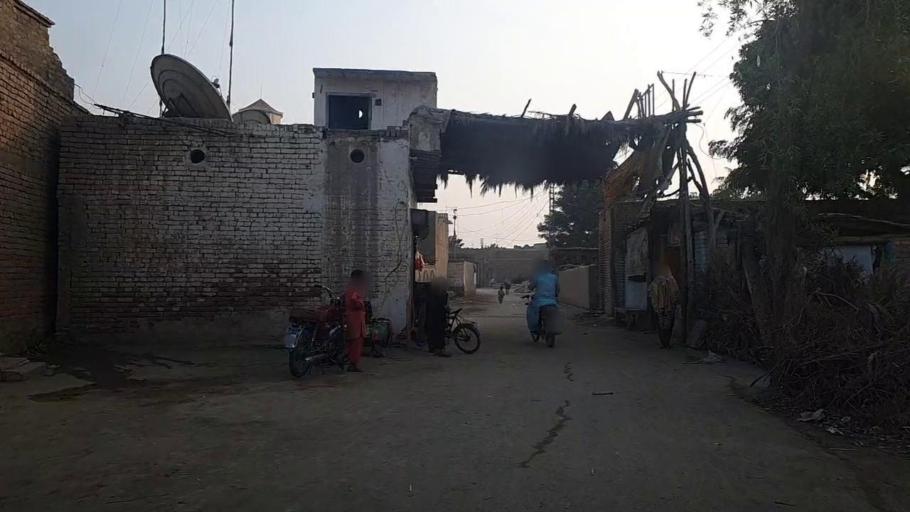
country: PK
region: Sindh
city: Kot Diji
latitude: 27.3769
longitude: 68.6659
